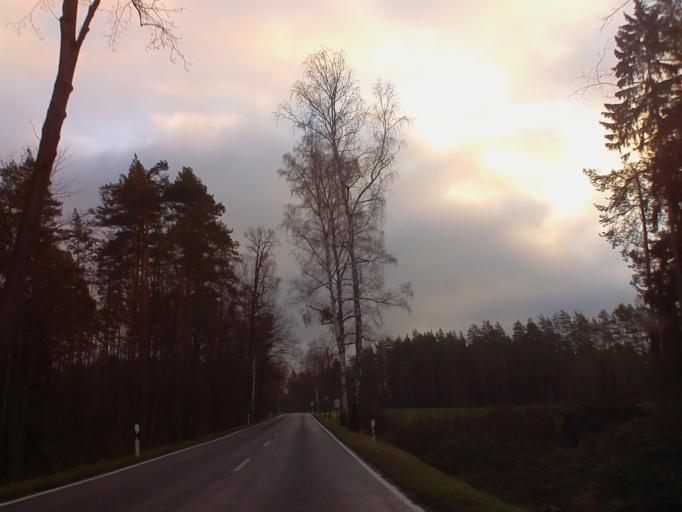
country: DE
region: Thuringia
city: Trockenborn-Wolfersdorf
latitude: 50.7534
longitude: 11.7086
